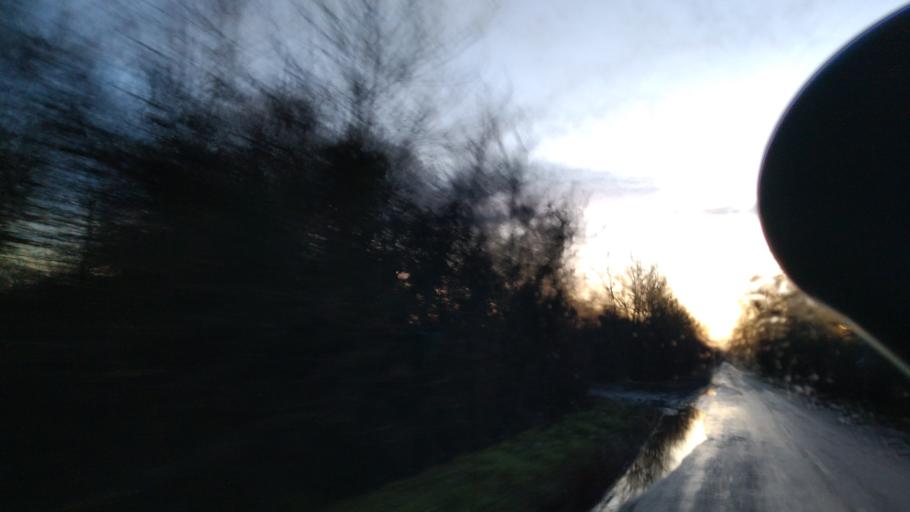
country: GB
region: England
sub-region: Borough of Swindon
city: Wanborough
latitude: 51.5850
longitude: -1.7136
